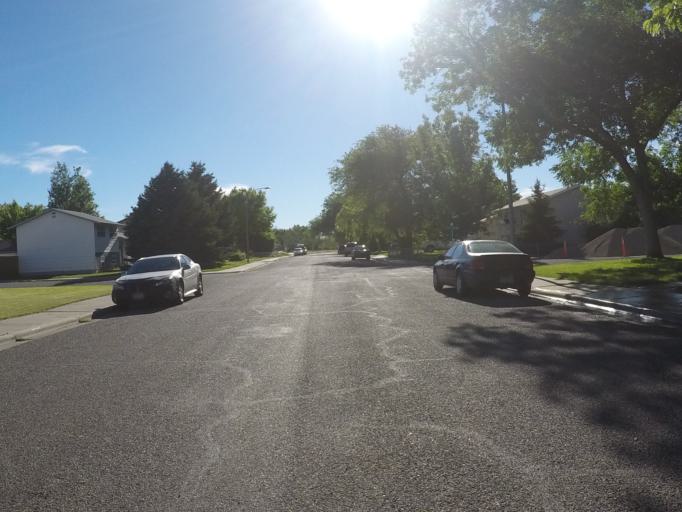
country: US
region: Montana
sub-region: Yellowstone County
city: Billings
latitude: 45.7737
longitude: -108.5837
